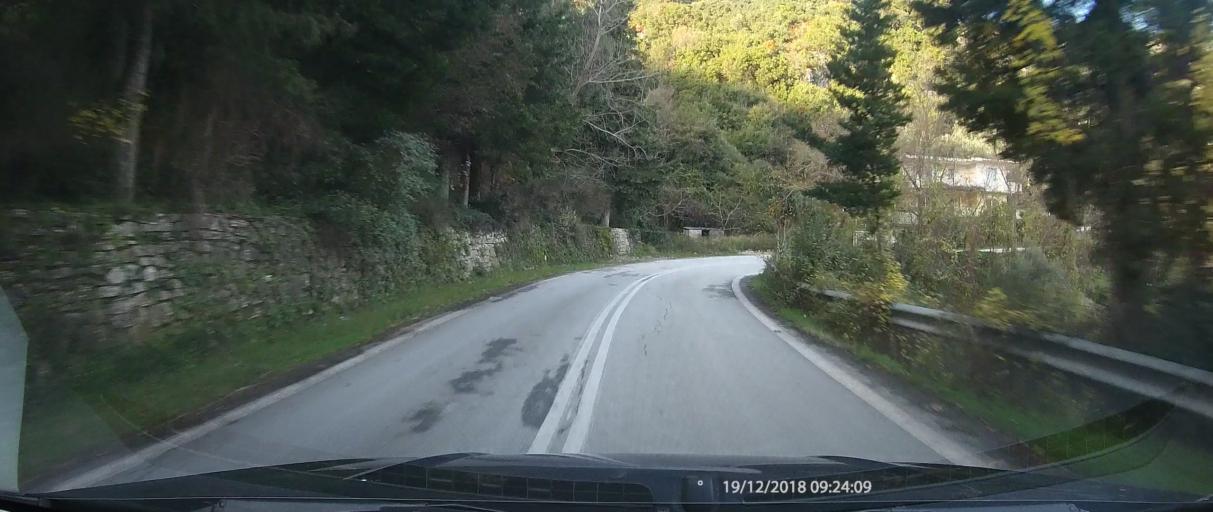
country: GR
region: Peloponnese
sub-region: Nomos Lakonias
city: Magoula
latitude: 37.0952
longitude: 22.3421
